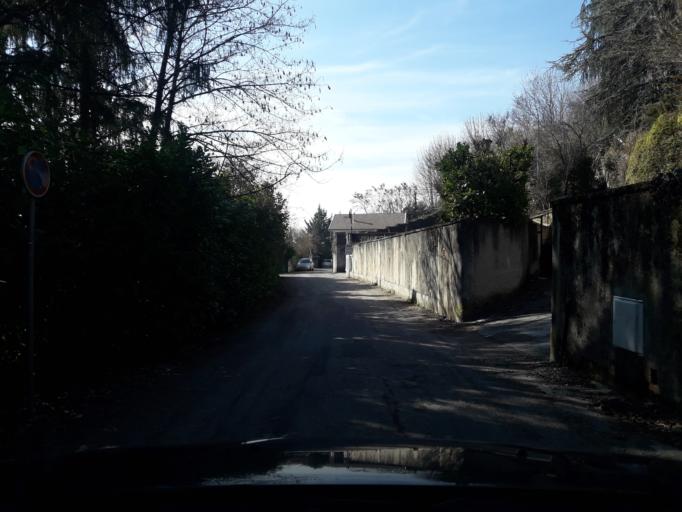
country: FR
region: Rhone-Alpes
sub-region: Departement de l'Isere
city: La Tronche
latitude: 45.2146
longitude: 5.7449
